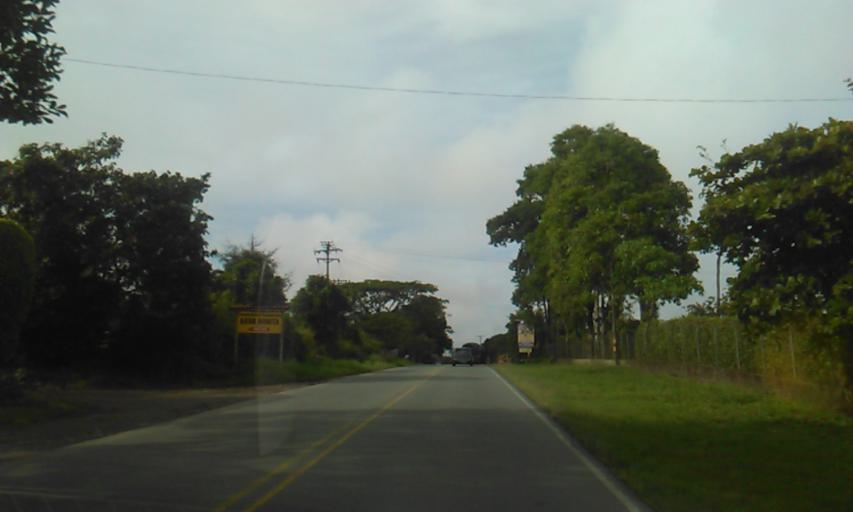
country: CO
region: Quindio
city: Cordoba
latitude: 4.4525
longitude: -75.7136
